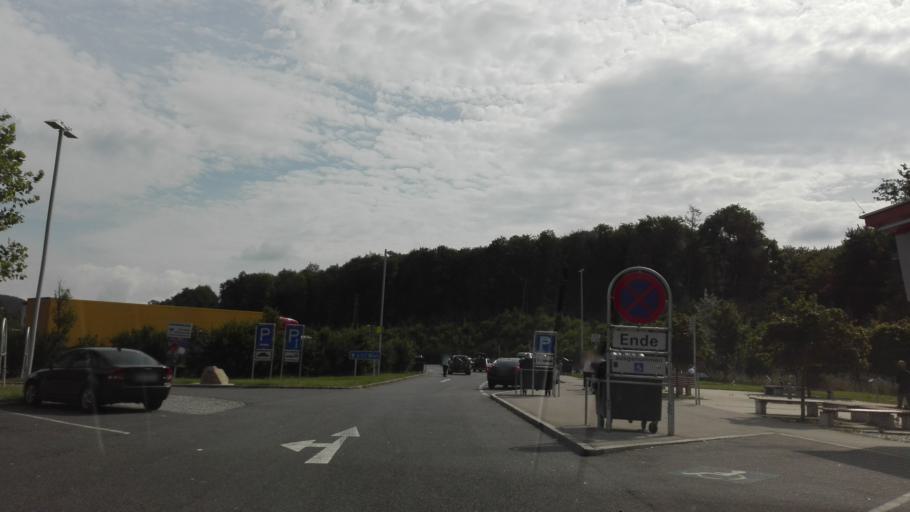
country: AT
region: Lower Austria
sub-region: Politischer Bezirk Modling
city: Gaaden
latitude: 48.0716
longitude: 16.2021
